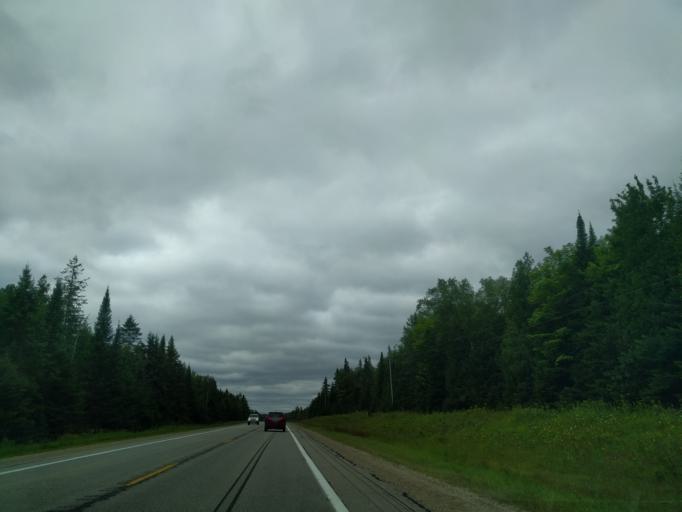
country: US
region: Michigan
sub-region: Delta County
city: Escanaba
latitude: 45.5705
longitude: -87.2534
